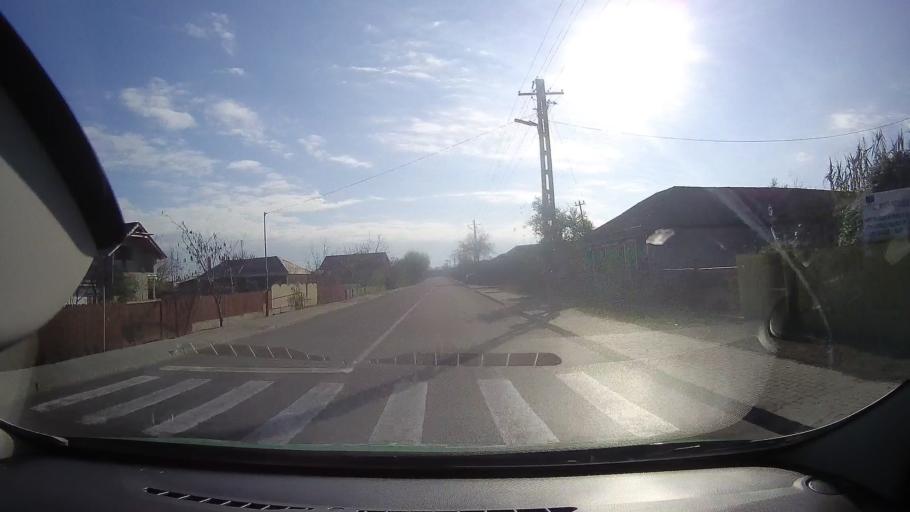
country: RO
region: Tulcea
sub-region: Comuna Murighiol
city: Murighiol
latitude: 45.0403
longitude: 29.1572
